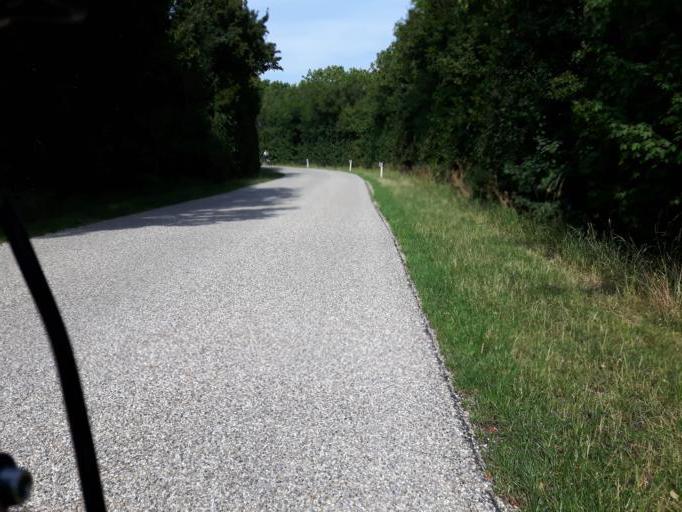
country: NL
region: Zeeland
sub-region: Gemeente Middelburg
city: Middelburg
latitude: 51.4743
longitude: 3.6310
